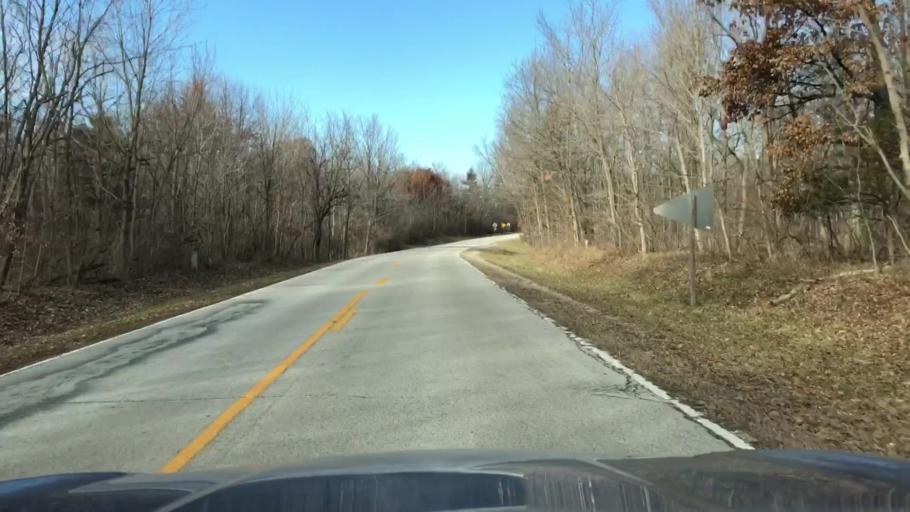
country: US
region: Illinois
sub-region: McLean County
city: Hudson
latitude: 40.6540
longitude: -88.9236
